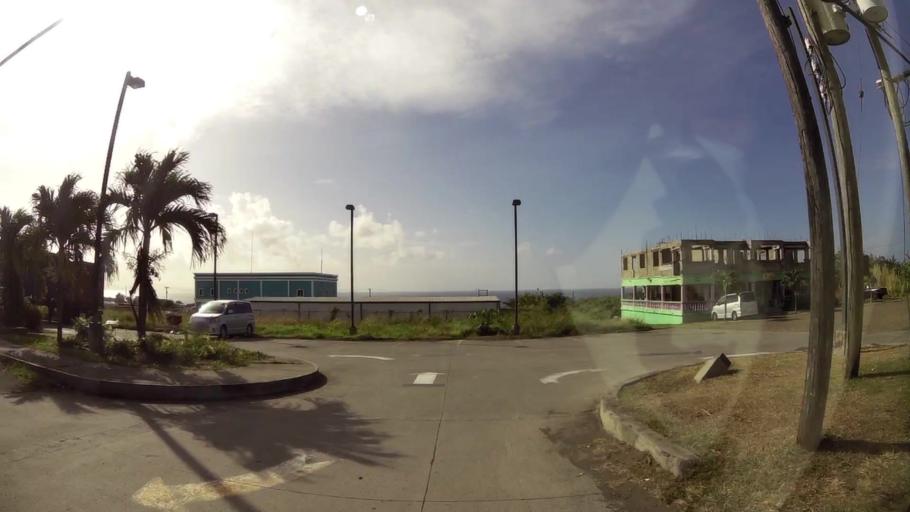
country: KN
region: Saint George Basseterre
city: Basseterre
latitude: 17.2964
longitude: -62.7406
